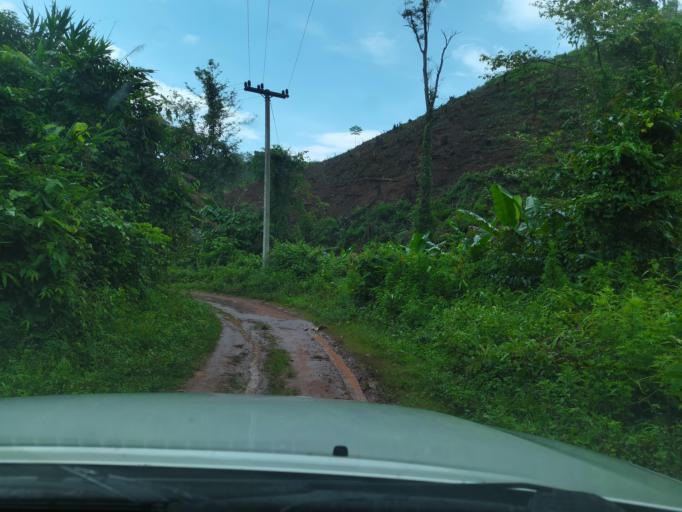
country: LA
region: Loungnamtha
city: Muang Nale
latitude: 20.5247
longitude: 101.0683
